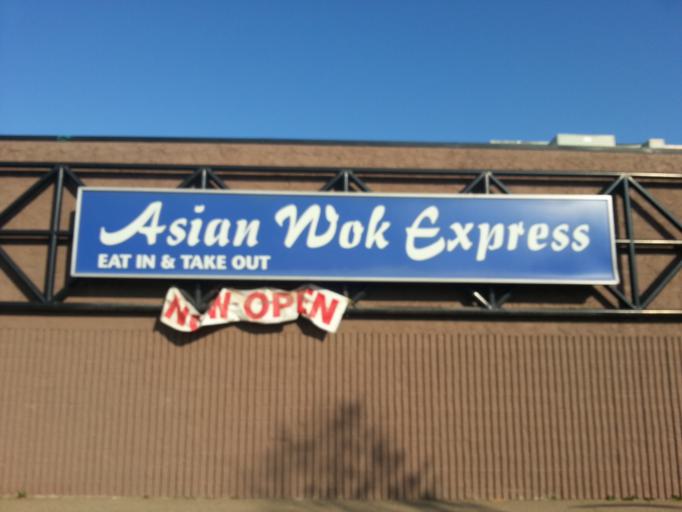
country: CA
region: Alberta
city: St. Albert
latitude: 53.6229
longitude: -113.6082
